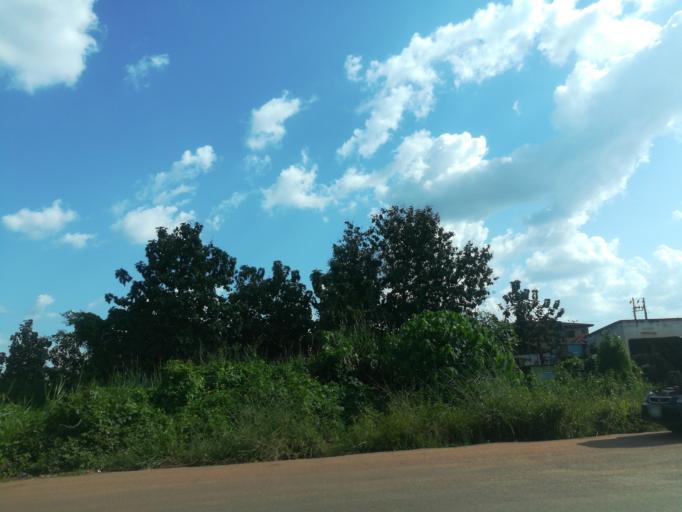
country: NG
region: Oyo
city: Egbeda
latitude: 7.4235
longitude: 3.9819
